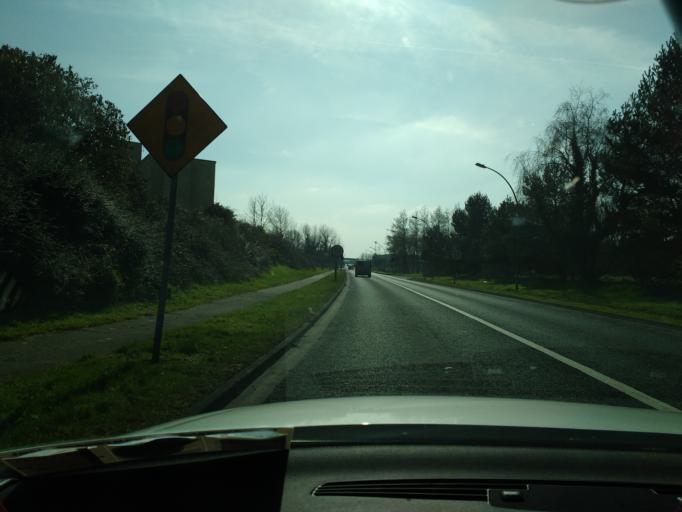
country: IE
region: Munster
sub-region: An Clar
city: Shannon
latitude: 52.6998
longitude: -8.8992
